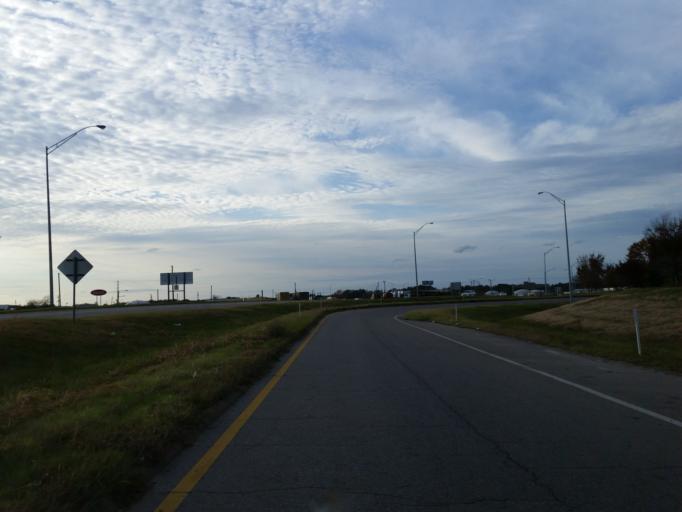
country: US
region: Mississippi
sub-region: Lauderdale County
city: Meridian
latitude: 32.3489
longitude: -88.7368
